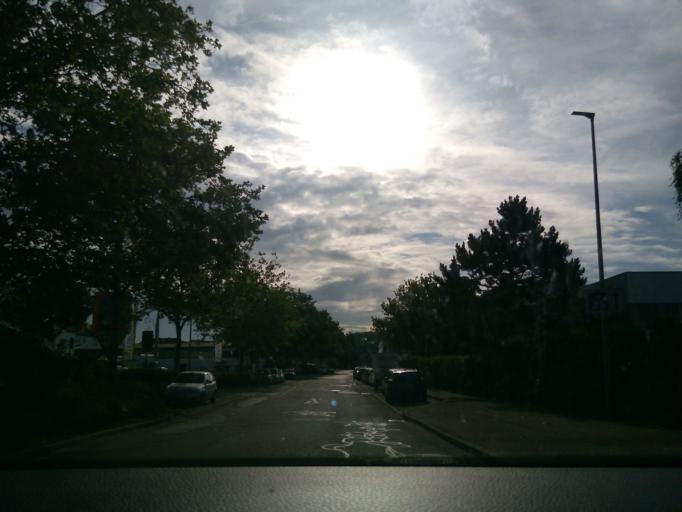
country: DE
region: Baden-Wuerttemberg
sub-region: Regierungsbezirk Stuttgart
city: Kuenzelsau
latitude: 49.2554
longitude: 9.6834
